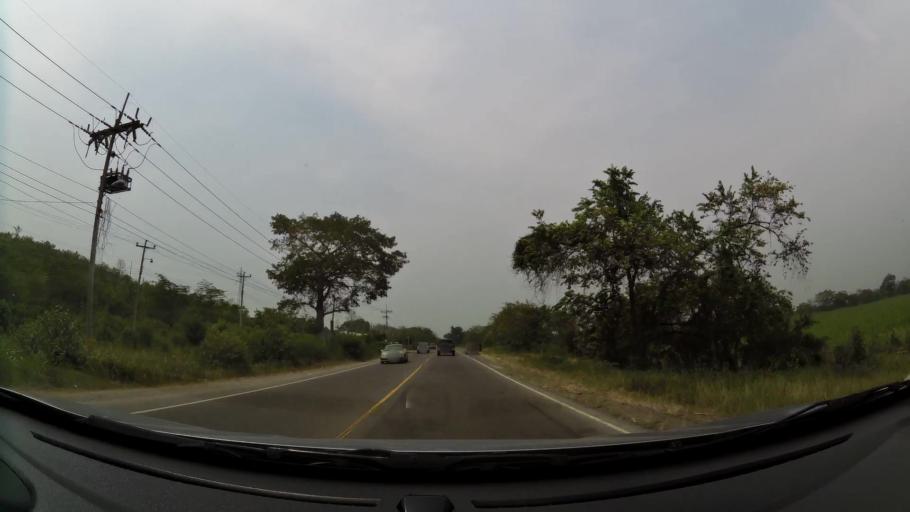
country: HN
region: Cortes
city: Potrerillos
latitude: 15.1828
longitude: -87.9621
